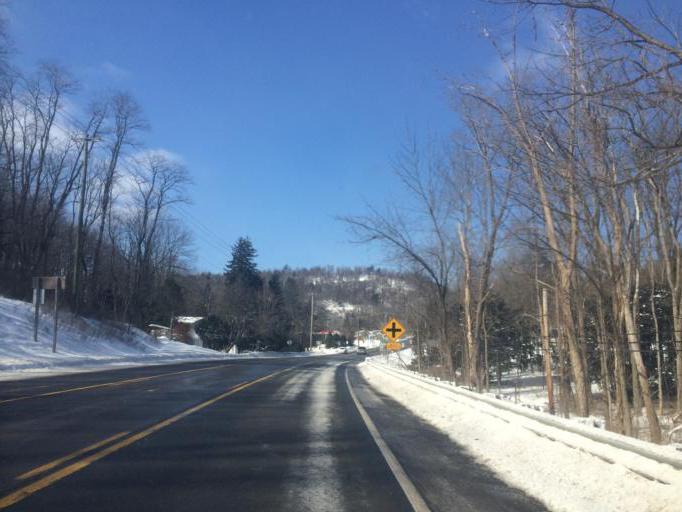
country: US
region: Pennsylvania
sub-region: Centre County
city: Park Forest Village
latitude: 40.8273
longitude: -77.9600
